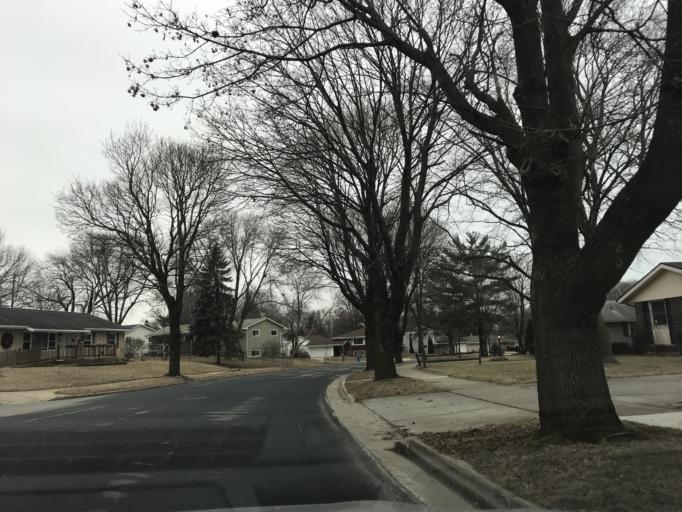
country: US
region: Wisconsin
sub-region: Dane County
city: Monona
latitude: 43.0866
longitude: -89.2933
